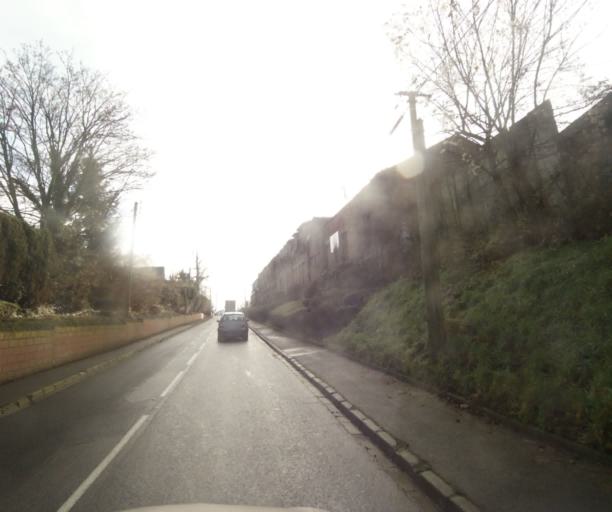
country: FR
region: Nord-Pas-de-Calais
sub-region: Departement du Nord
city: Artres
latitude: 50.2884
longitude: 3.5433
